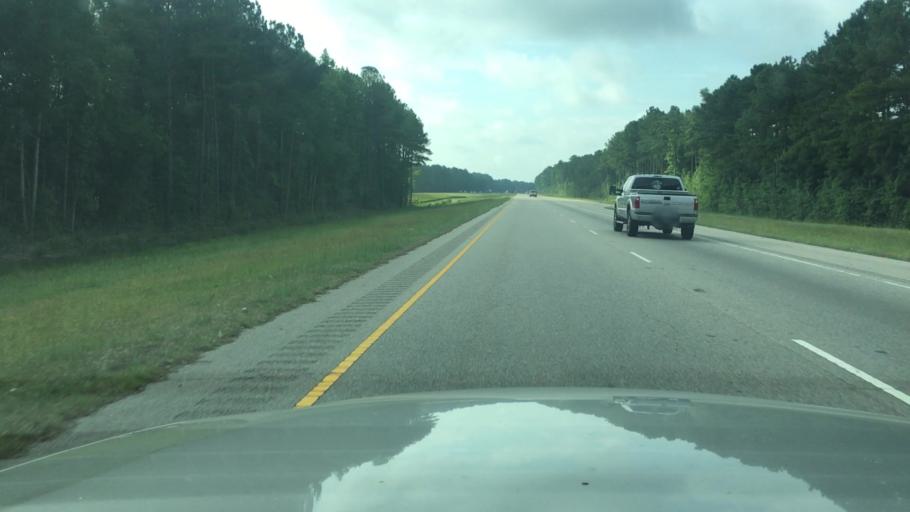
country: US
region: North Carolina
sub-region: Cumberland County
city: Fayetteville
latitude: 34.9735
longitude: -78.8547
